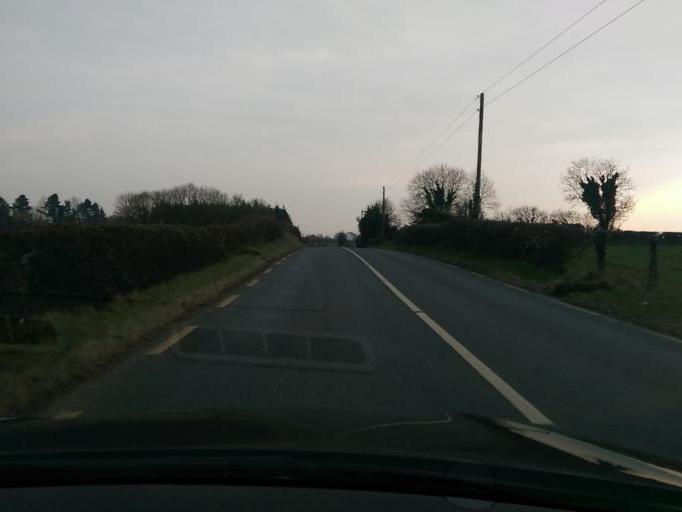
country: IE
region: Leinster
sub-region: An Longfort
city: Ballymahon
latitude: 53.5129
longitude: -7.8238
